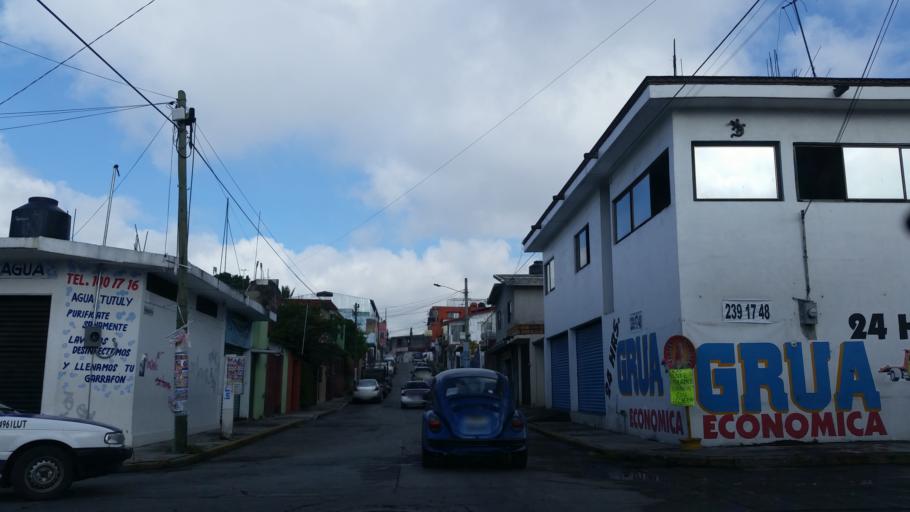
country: MX
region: Morelos
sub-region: Cuernavaca
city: Cuernavaca
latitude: 18.9190
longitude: -99.2054
